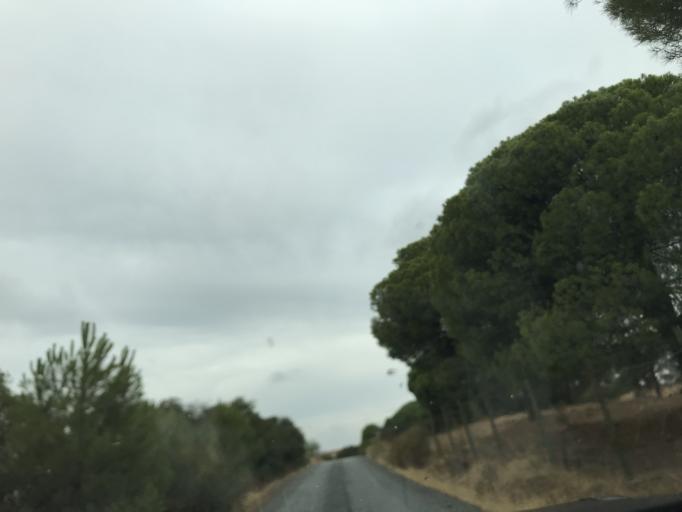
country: ES
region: Andalusia
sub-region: Provincia de Sevilla
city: Villanueva del Rio y Minas
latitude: 37.6721
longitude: -5.7365
